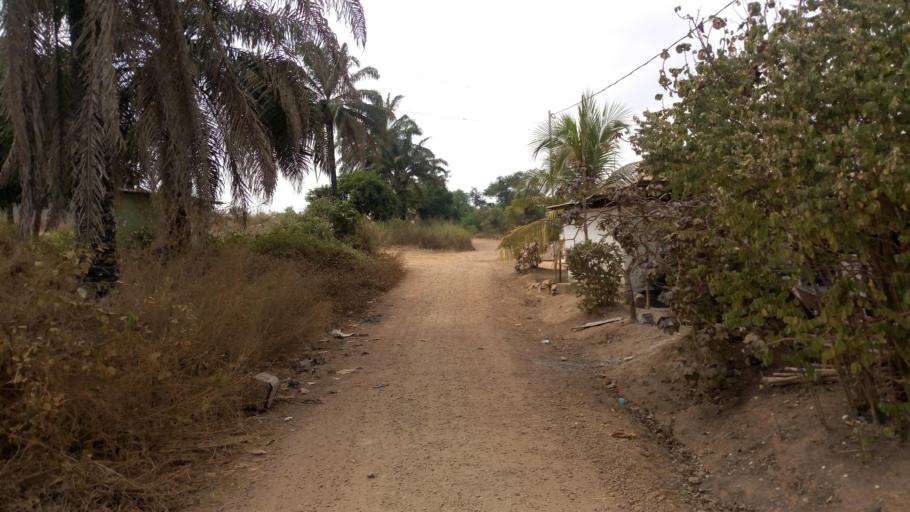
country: SL
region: Southern Province
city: Mogbwemo
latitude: 7.7963
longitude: -12.2999
